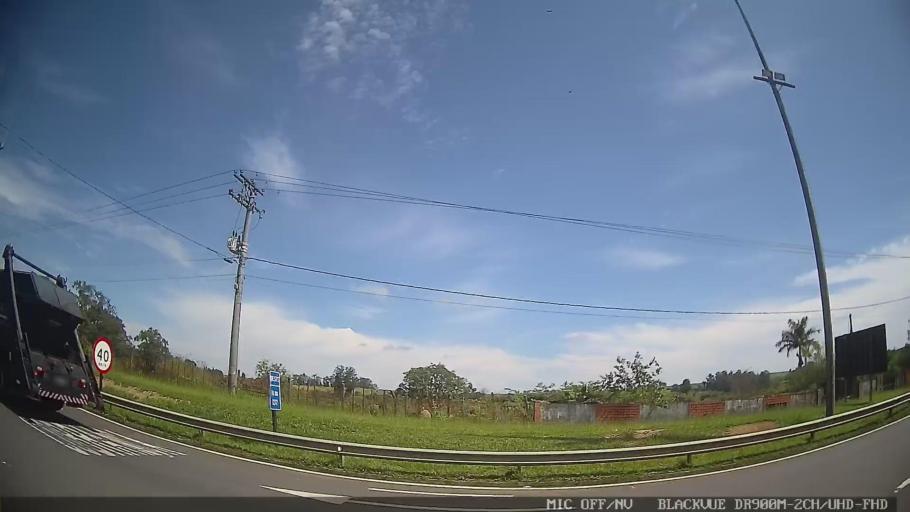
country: BR
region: Sao Paulo
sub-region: Porto Feliz
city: Porto Feliz
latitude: -23.2272
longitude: -47.5616
